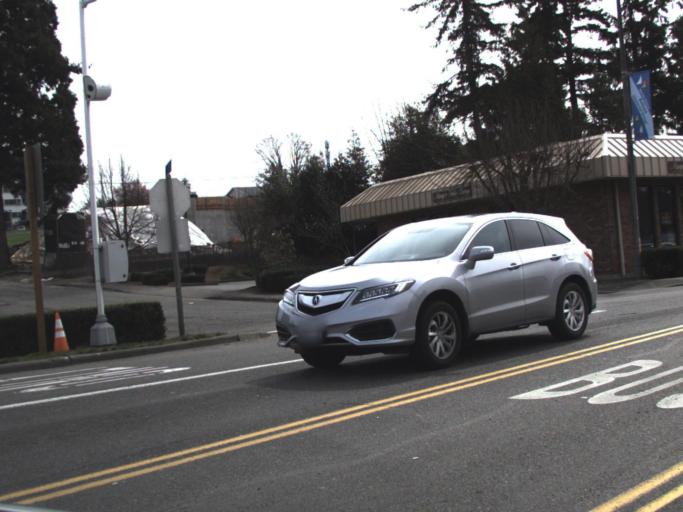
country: US
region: Washington
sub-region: King County
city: Des Moines
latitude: 47.4071
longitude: -122.3248
